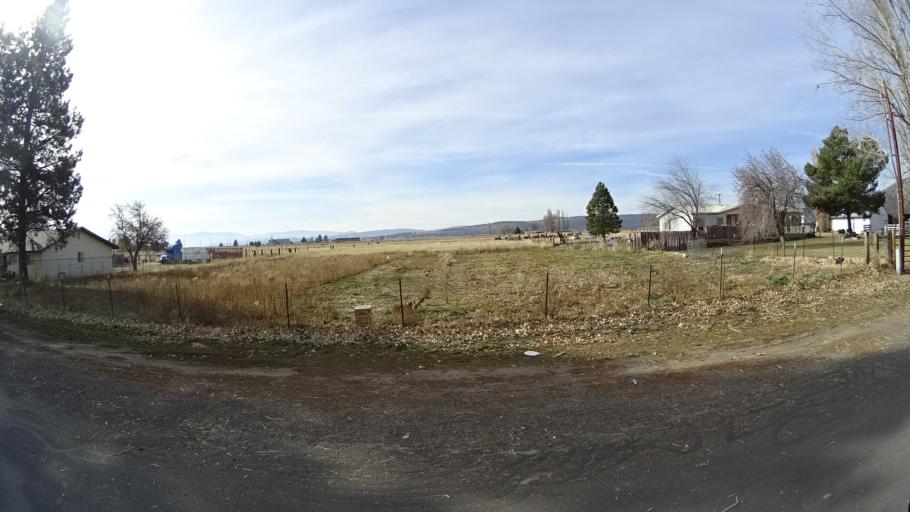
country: US
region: Oregon
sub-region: Klamath County
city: Klamath Falls
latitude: 41.9696
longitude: -121.9214
